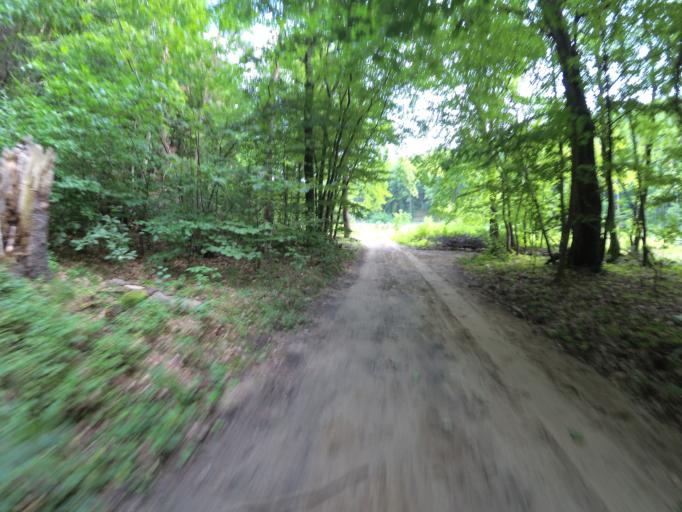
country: PL
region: Pomeranian Voivodeship
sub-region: Gdynia
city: Wielki Kack
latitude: 54.4892
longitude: 18.4463
